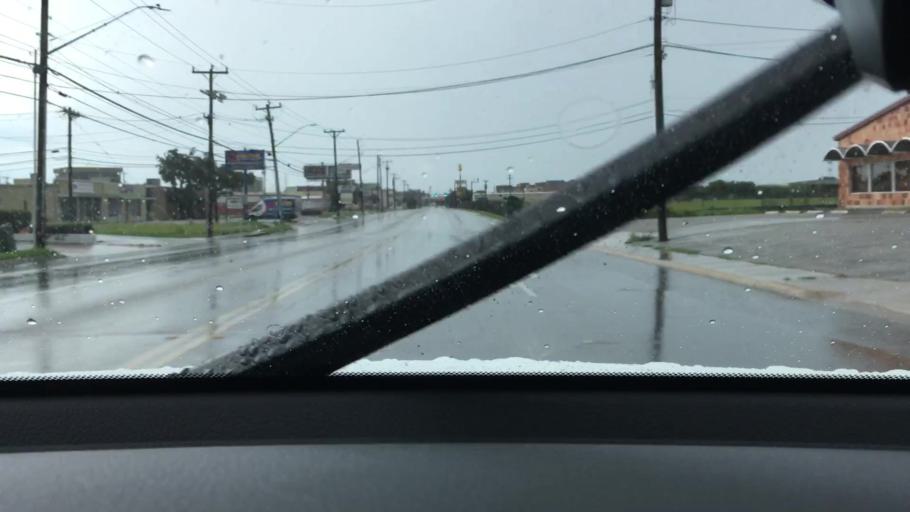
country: US
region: Texas
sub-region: Bexar County
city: Alamo Heights
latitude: 29.5237
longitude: -98.4577
